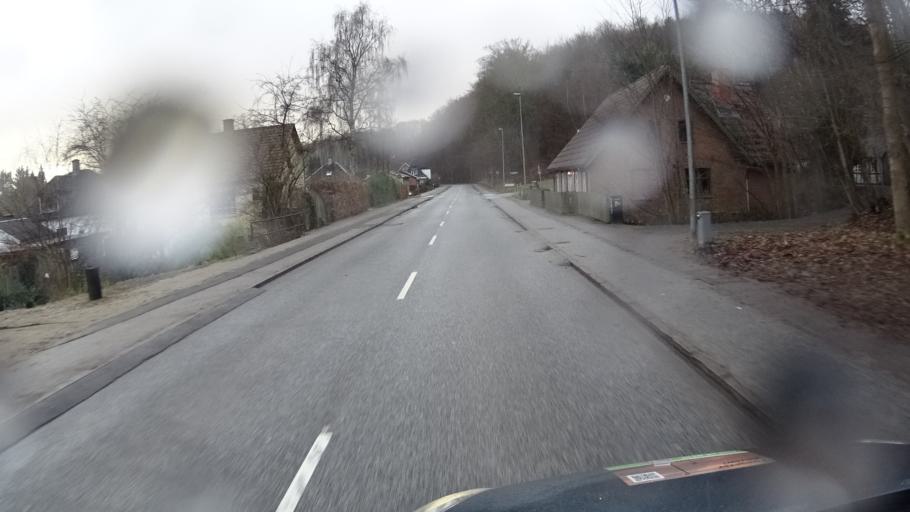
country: DK
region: South Denmark
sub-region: Vejle Kommune
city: Vejle
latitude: 55.7388
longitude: 9.5334
